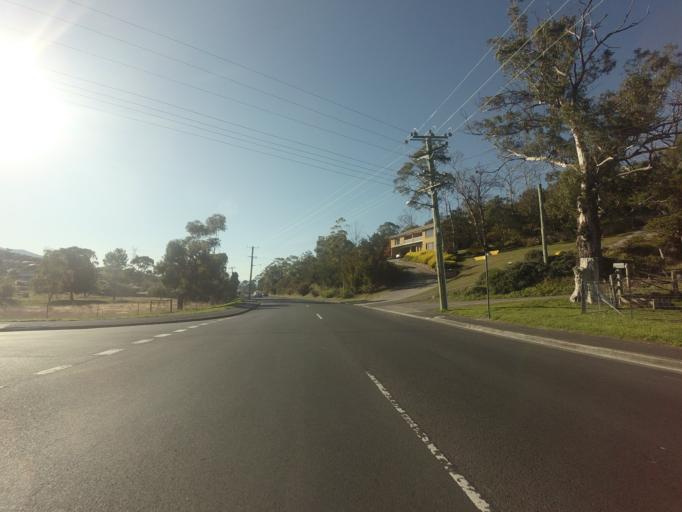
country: AU
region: Tasmania
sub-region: Glenorchy
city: West Moonah
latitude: -42.8530
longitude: 147.2682
